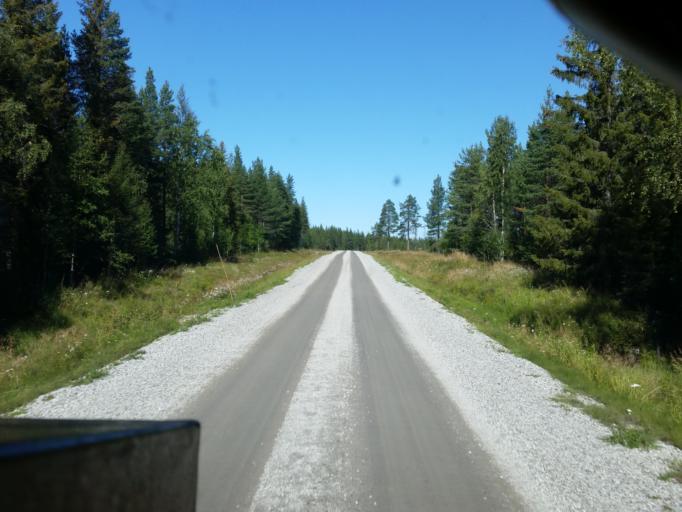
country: SE
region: Vaesterbotten
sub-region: Skelleftea Kommun
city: Storvik
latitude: 65.3196
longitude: 20.6083
